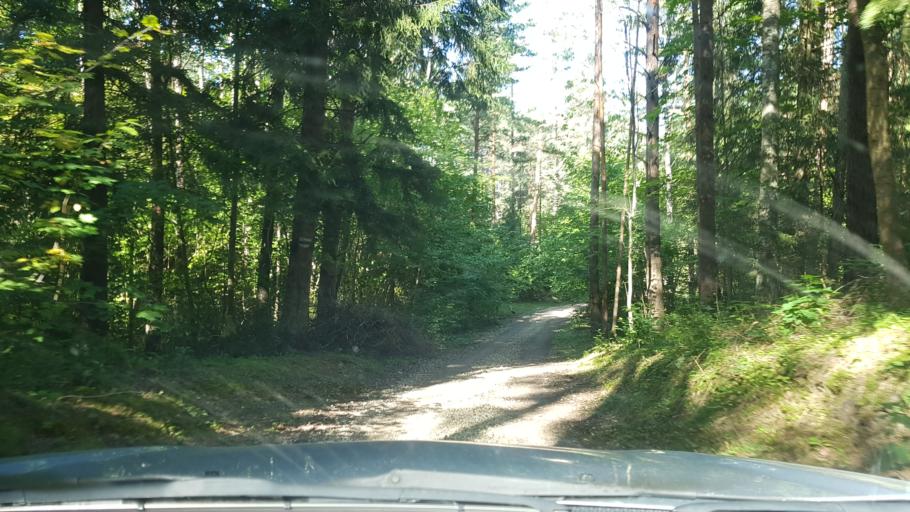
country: EE
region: Ida-Virumaa
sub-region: Sillamaee linn
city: Sillamae
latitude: 59.3983
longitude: 27.8787
